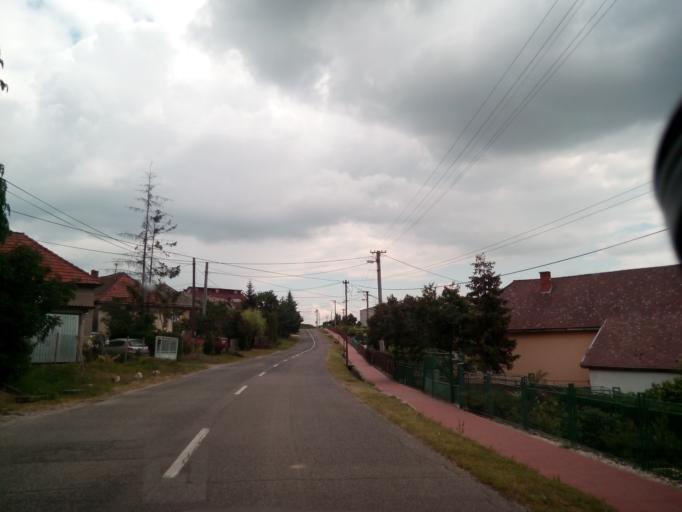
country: SK
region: Kosicky
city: Secovce
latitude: 48.6137
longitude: 21.5323
